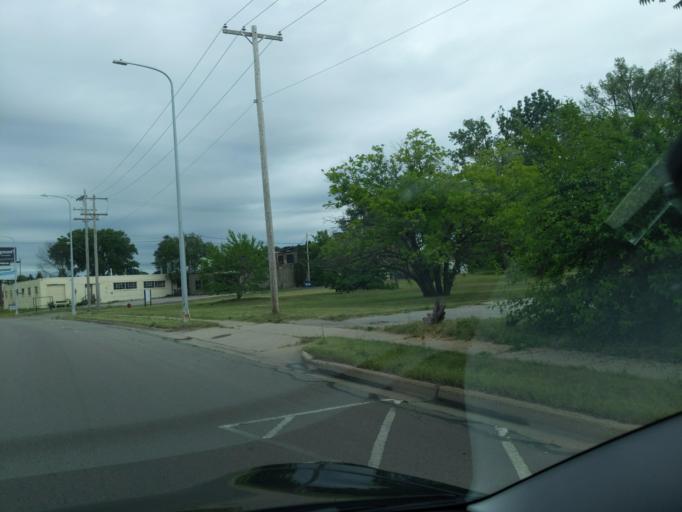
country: US
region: Michigan
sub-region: Muskegon County
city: Muskegon
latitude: 43.2288
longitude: -86.2641
